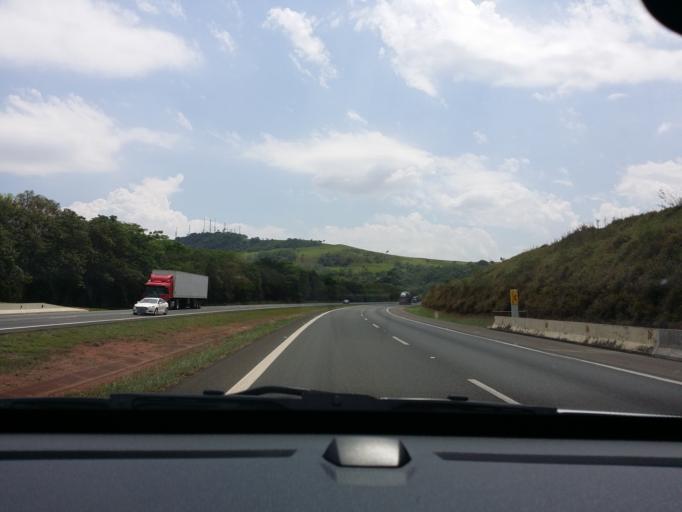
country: BR
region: Sao Paulo
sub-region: Limeira
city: Limeira
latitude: -22.5497
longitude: -47.4620
